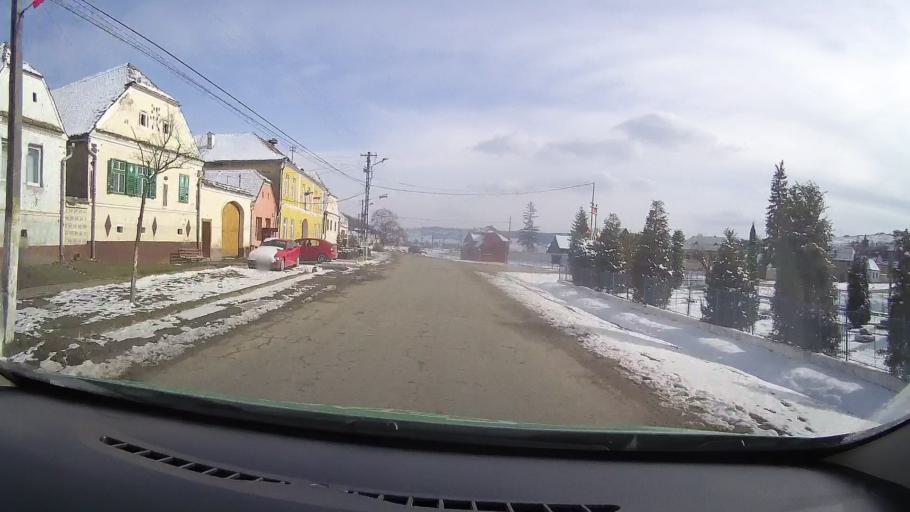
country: RO
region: Sibiu
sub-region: Comuna Iacobeni
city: Iacobeni
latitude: 46.0512
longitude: 24.7165
